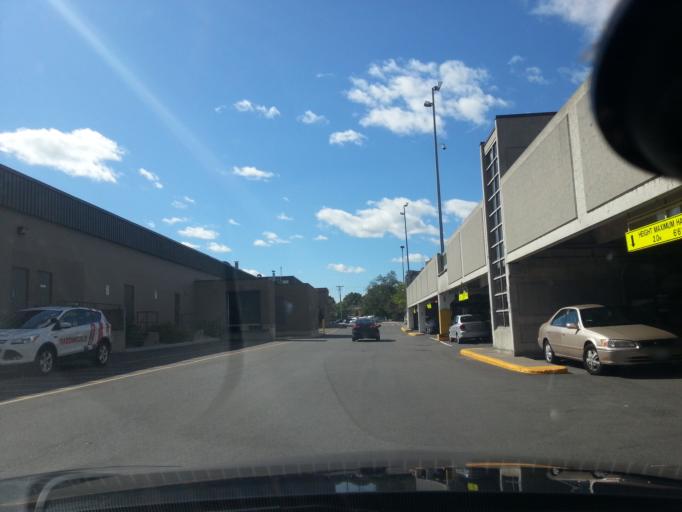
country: CA
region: Ontario
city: Ottawa
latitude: 45.3737
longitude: -75.7680
